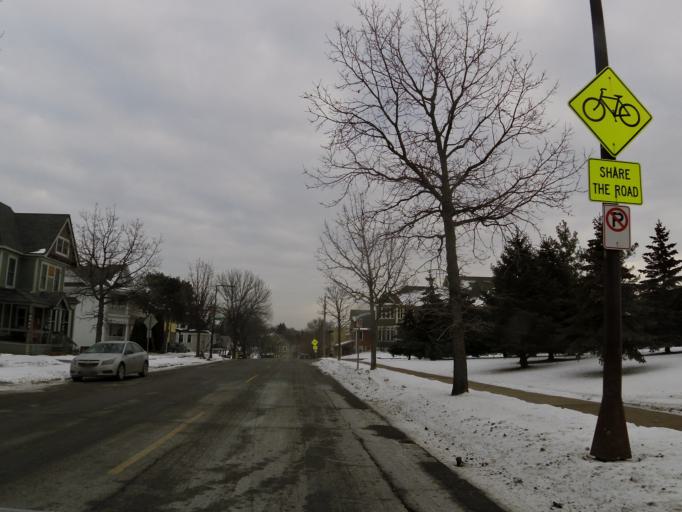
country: US
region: Minnesota
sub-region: Ramsey County
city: Saint Paul
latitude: 44.9589
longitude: -93.1017
